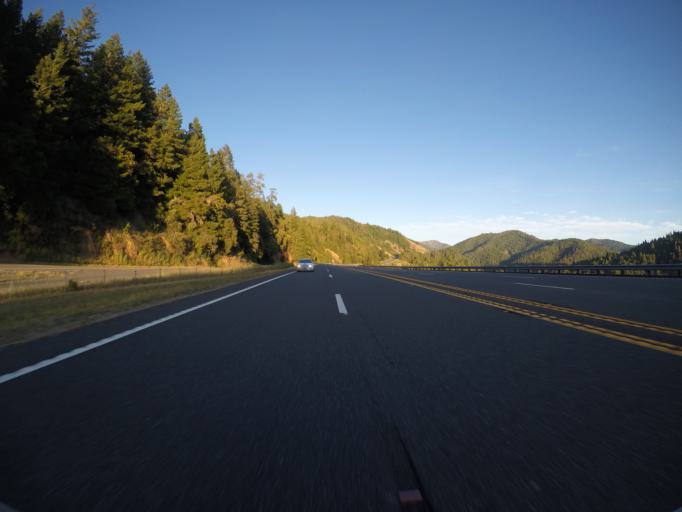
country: US
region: California
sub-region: Mendocino County
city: Laytonville
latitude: 39.8384
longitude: -123.6872
